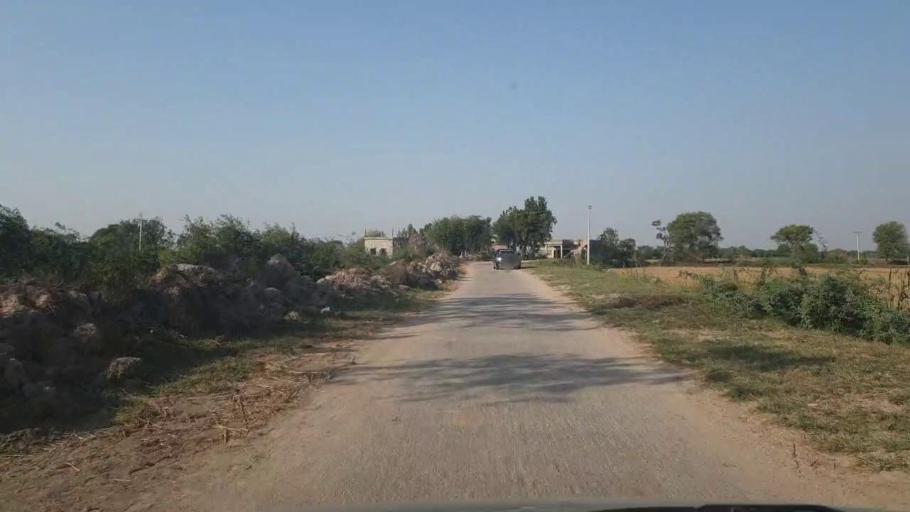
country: PK
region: Sindh
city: Badin
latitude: 24.6561
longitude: 68.8113
